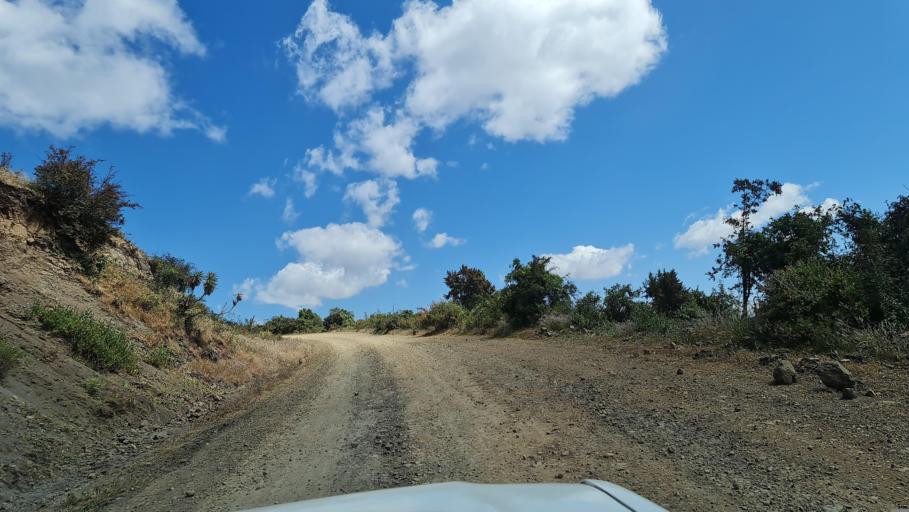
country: ET
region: Amhara
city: Debark'
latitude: 13.2215
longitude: 38.0278
